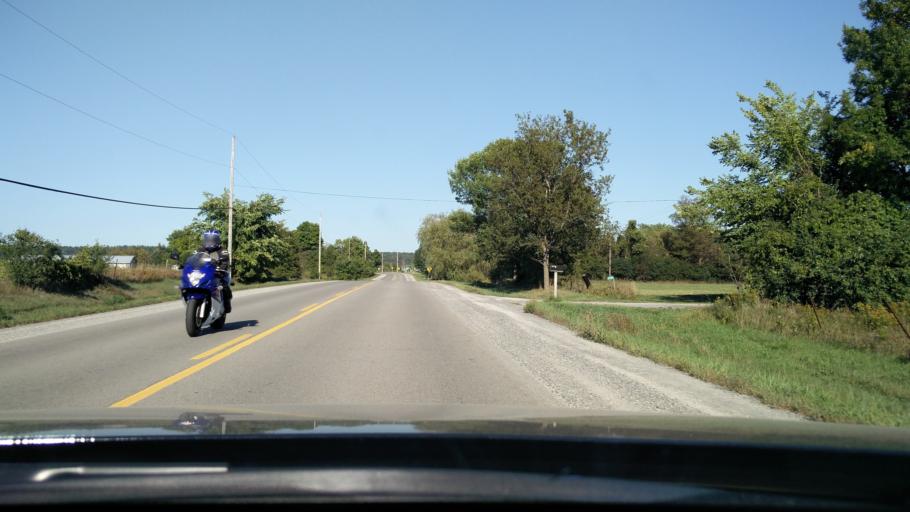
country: CA
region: Ontario
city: Perth
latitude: 44.6713
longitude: -76.4244
